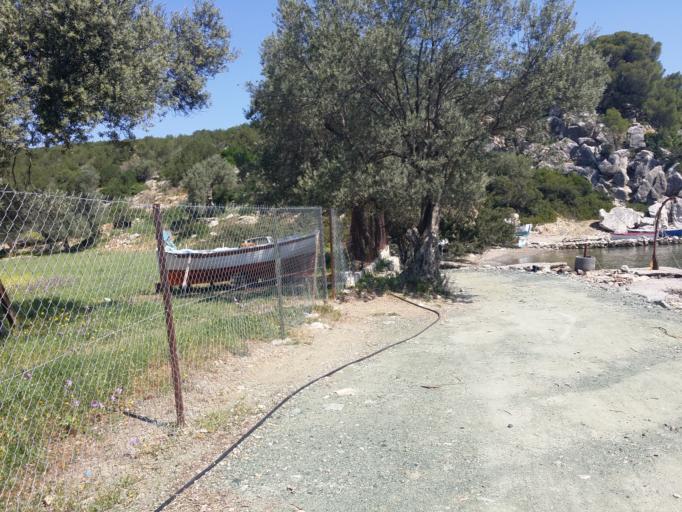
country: GR
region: Attica
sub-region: Nomos Piraios
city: Poros
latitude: 37.5318
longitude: 23.4828
